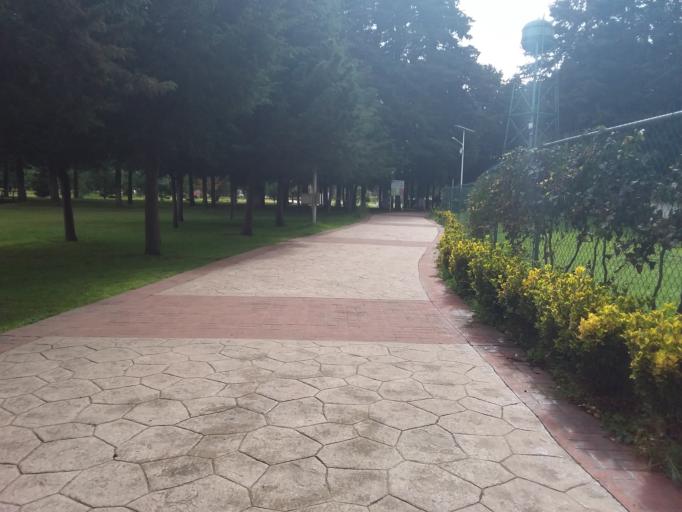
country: MX
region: Mexico
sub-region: Metepec
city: San Salvador Tizatlalli
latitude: 19.2499
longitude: -99.5808
